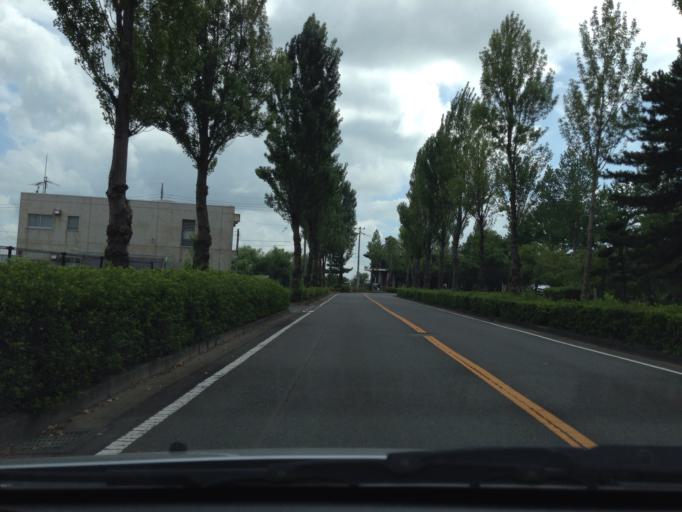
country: JP
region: Ibaraki
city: Ami
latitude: 36.0661
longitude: 140.2185
